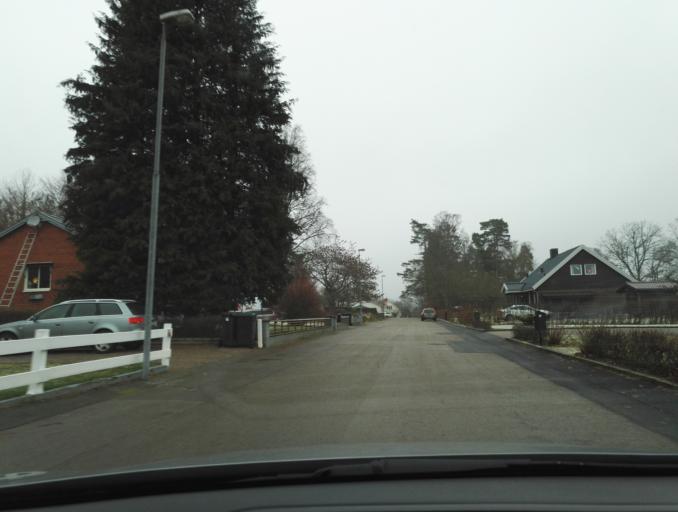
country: SE
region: Kronoberg
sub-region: Vaxjo Kommun
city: Vaexjoe
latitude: 56.9009
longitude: 14.7356
